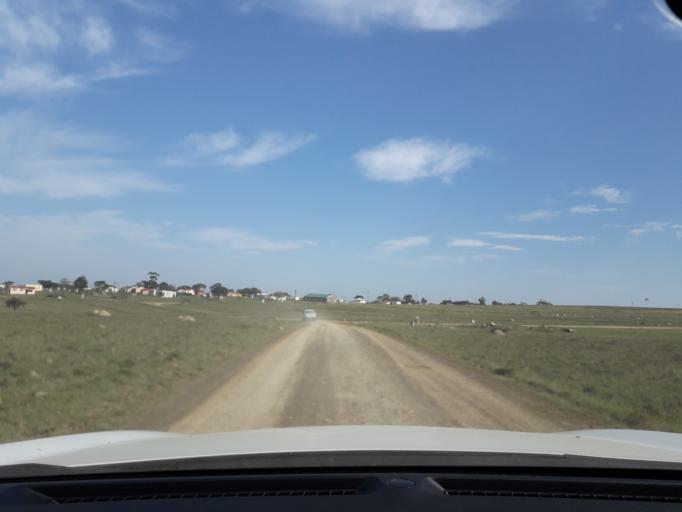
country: ZA
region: Eastern Cape
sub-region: Buffalo City Metropolitan Municipality
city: Bhisho
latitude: -33.0057
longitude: 27.3111
